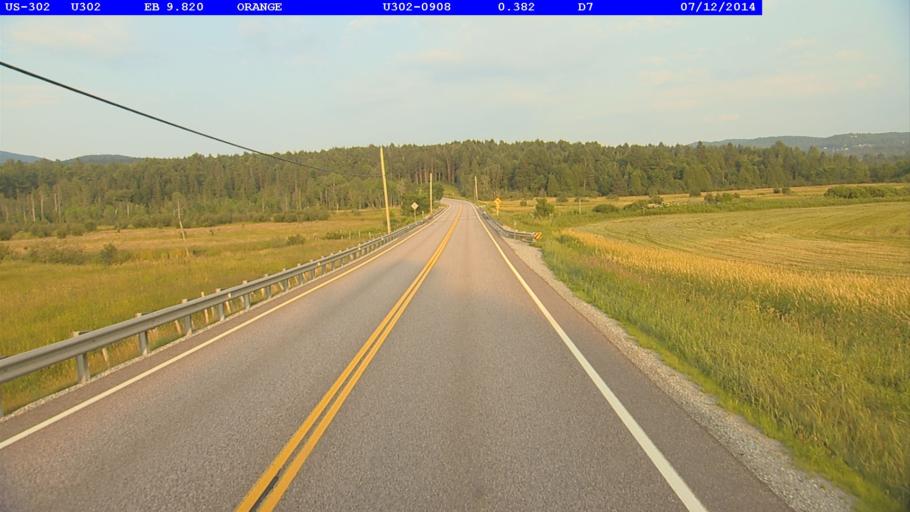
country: US
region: Vermont
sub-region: Washington County
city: South Barre
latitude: 44.1522
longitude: -72.4294
